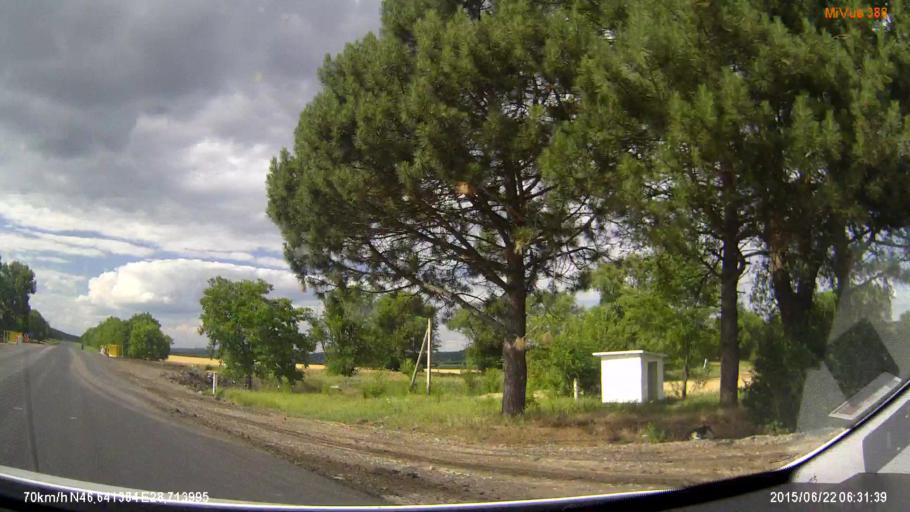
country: MD
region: Cimislia
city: Cimislia
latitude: 46.6411
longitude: 28.7142
